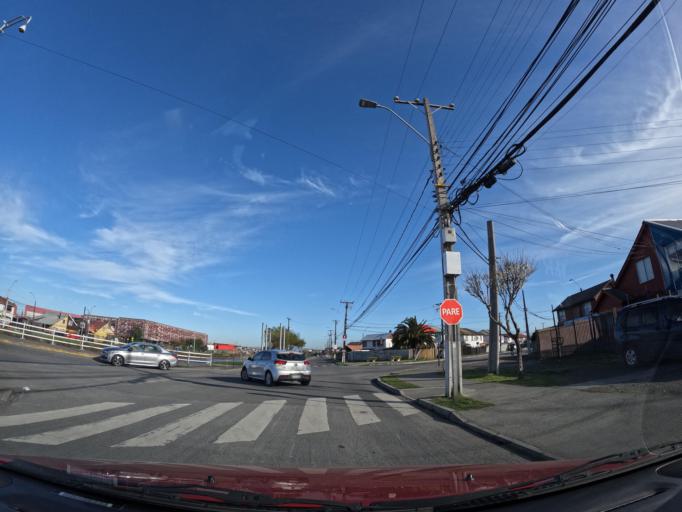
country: CL
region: Biobio
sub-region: Provincia de Concepcion
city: Talcahuano
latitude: -36.7506
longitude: -73.0849
